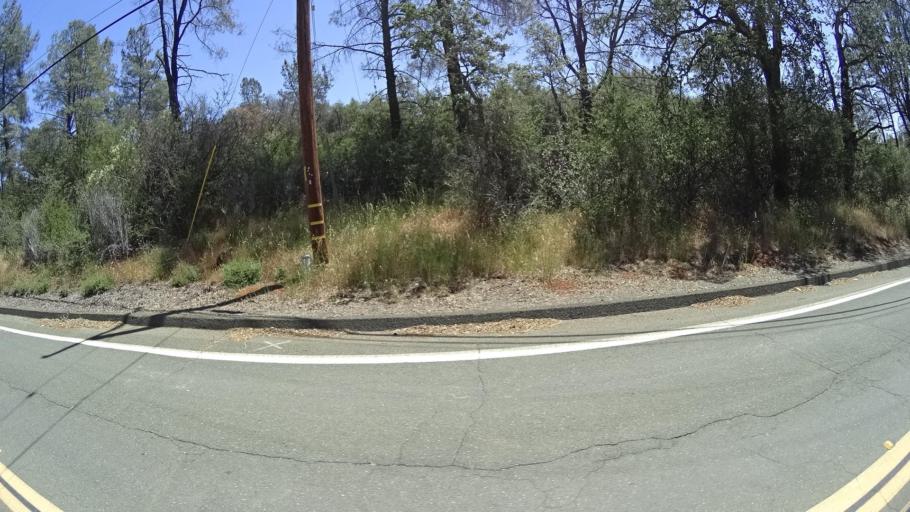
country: US
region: California
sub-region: Lake County
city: Hidden Valley Lake
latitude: 38.8235
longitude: -122.5461
